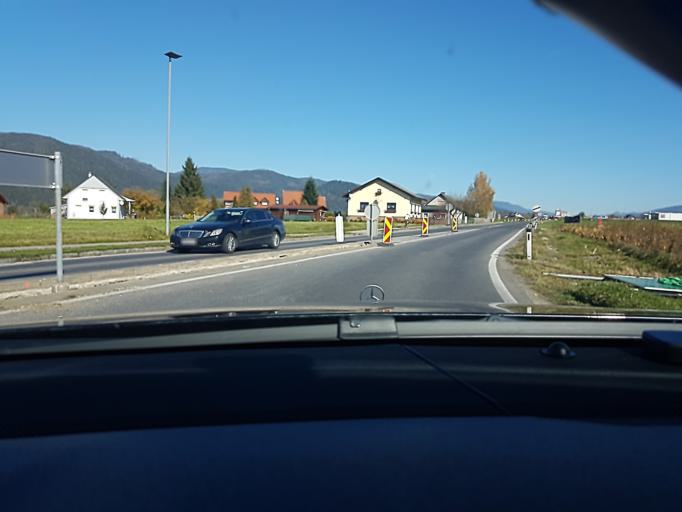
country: AT
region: Styria
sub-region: Politischer Bezirk Bruck-Muerzzuschlag
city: Mitterdorf im Muerztal
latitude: 47.5377
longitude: 15.5272
